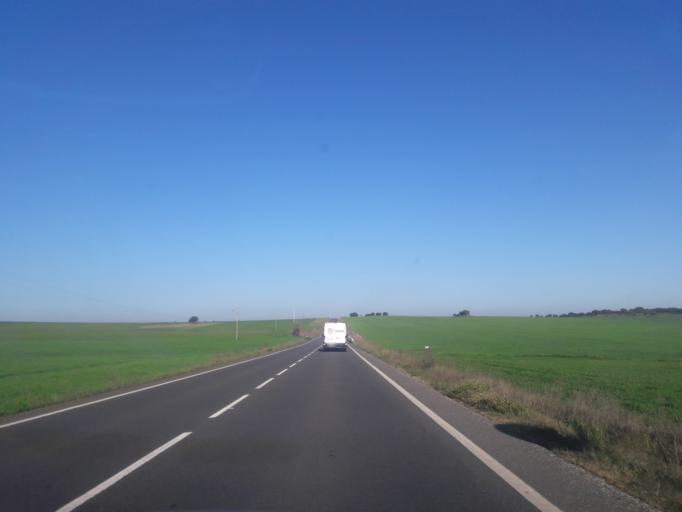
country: ES
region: Castille and Leon
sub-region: Provincia de Salamanca
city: Villarmayor
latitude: 41.0068
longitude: -5.9468
